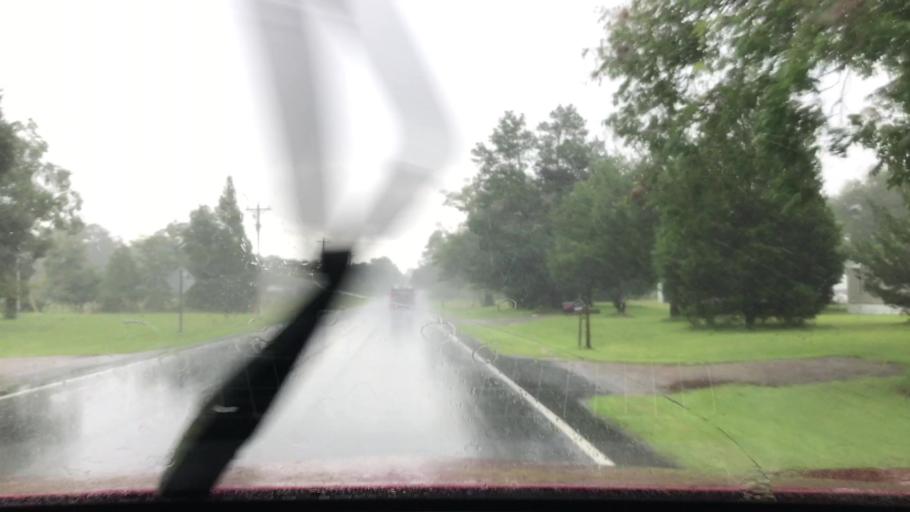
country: US
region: South Carolina
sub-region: Horry County
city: Red Hill
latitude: 33.9021
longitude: -78.8918
